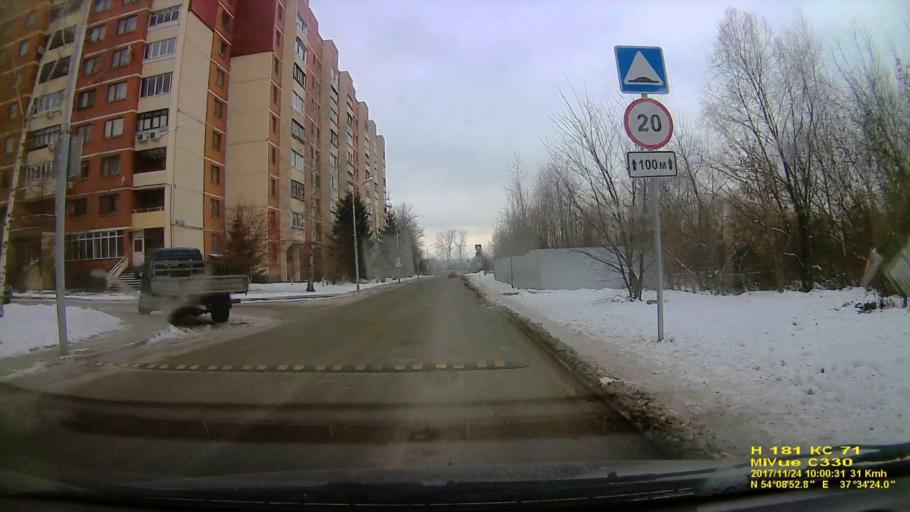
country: RU
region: Tula
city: Mendeleyevskiy
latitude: 54.1481
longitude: 37.5732
